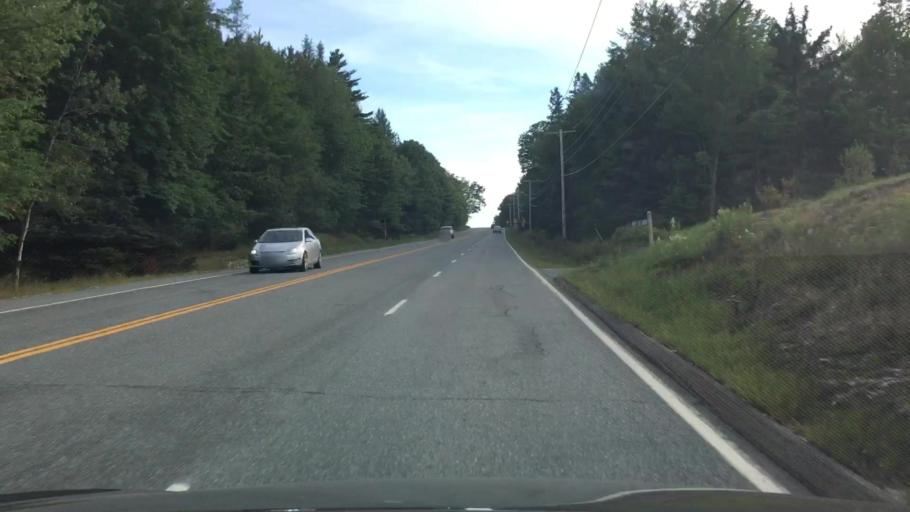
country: US
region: Maine
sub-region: Hancock County
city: Surry
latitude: 44.4926
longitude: -68.5079
